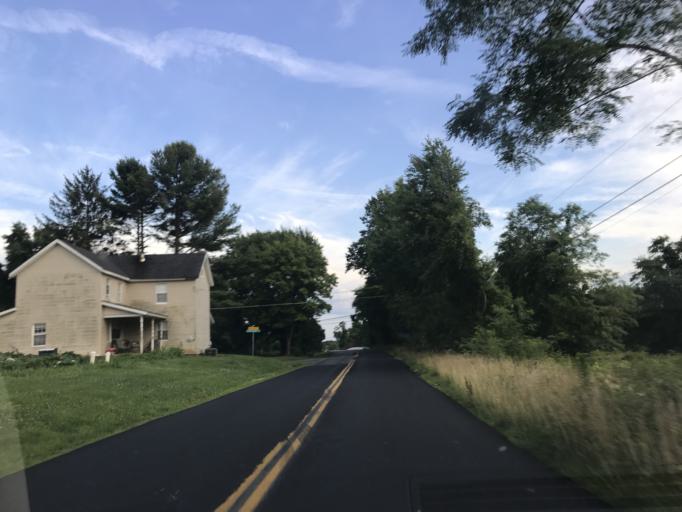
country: US
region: Maryland
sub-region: Harford County
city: Aberdeen
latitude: 39.5151
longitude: -76.2071
